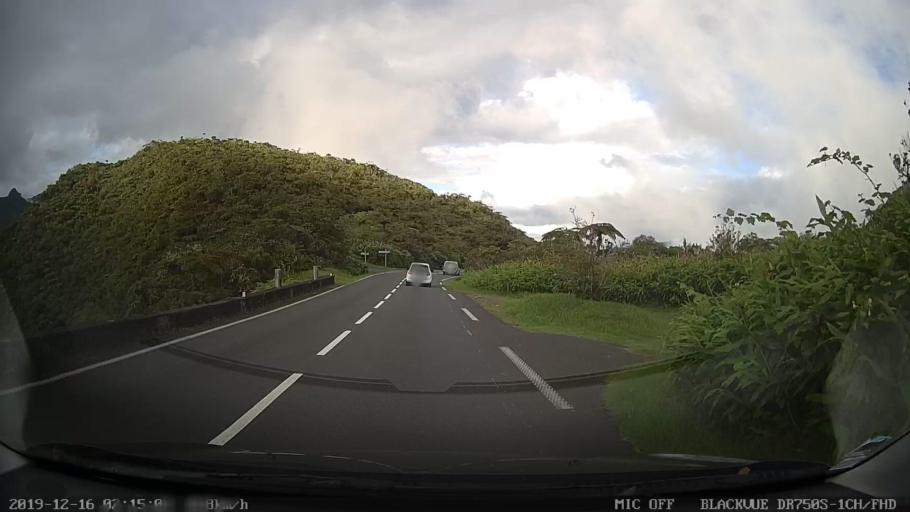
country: RE
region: Reunion
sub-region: Reunion
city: Cilaos
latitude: -21.1577
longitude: 55.5968
